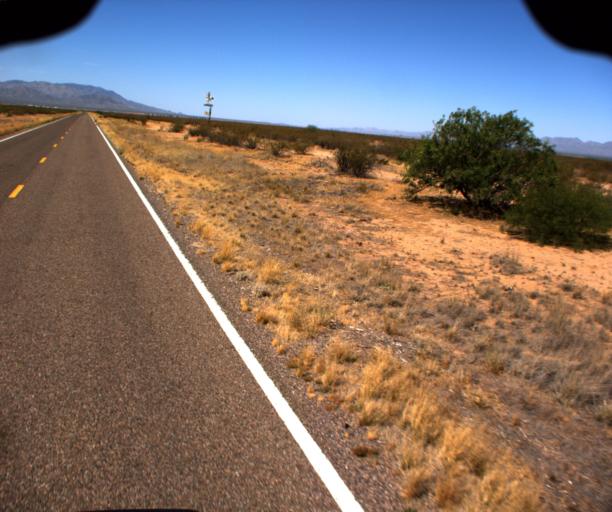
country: US
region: Arizona
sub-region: Yavapai County
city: Congress
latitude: 33.9994
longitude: -113.1226
